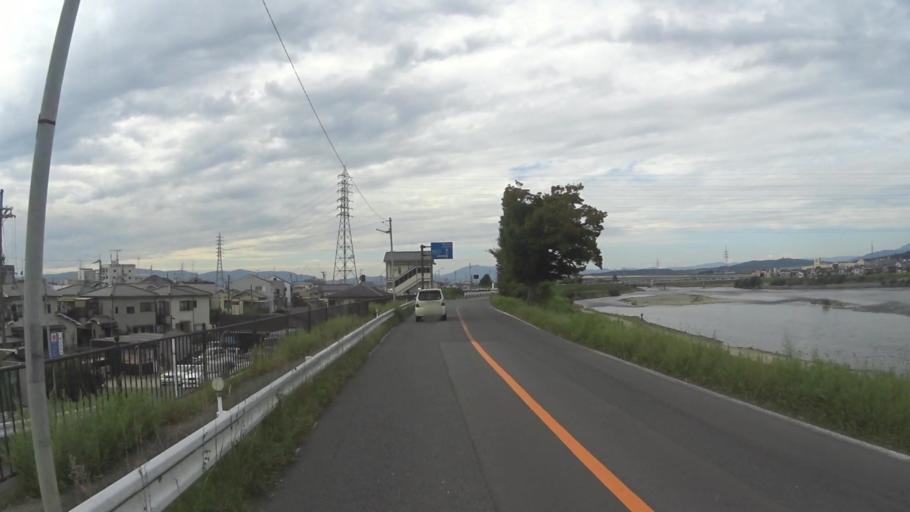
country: JP
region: Kyoto
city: Uji
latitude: 34.8946
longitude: 135.8033
